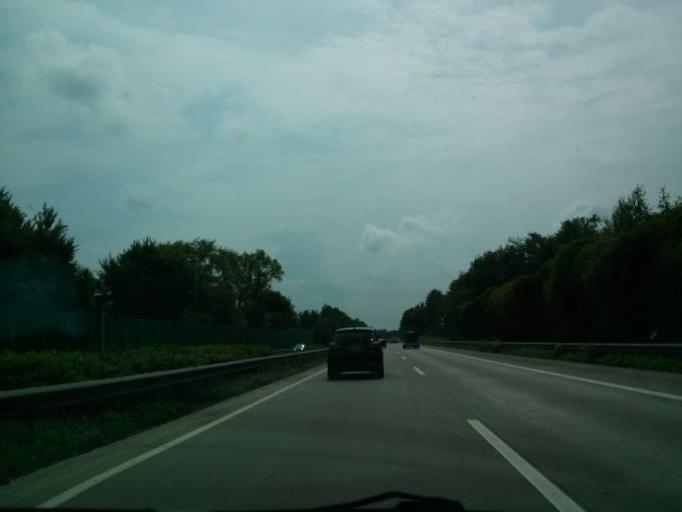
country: DE
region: Lower Saxony
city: Schiffdorf
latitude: 53.5224
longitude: 8.6249
